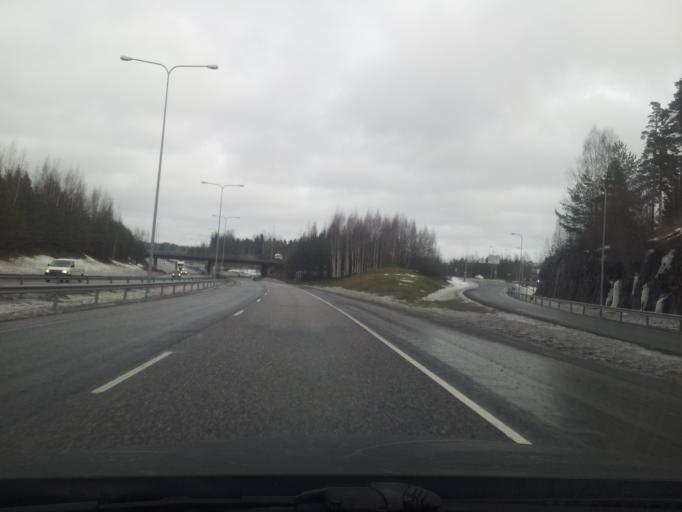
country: FI
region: Uusimaa
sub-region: Helsinki
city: Espoo
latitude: 60.2087
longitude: 24.6296
